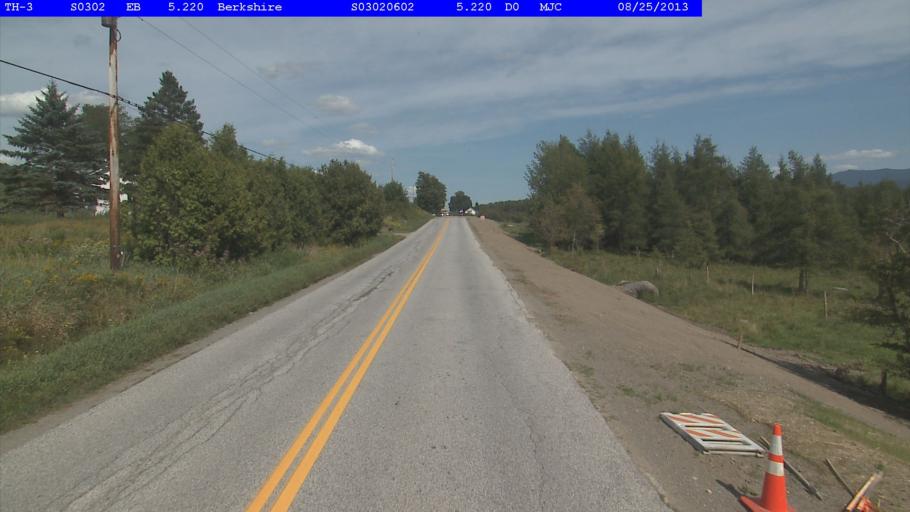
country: US
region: Vermont
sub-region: Franklin County
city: Richford
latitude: 44.9836
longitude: -72.7167
